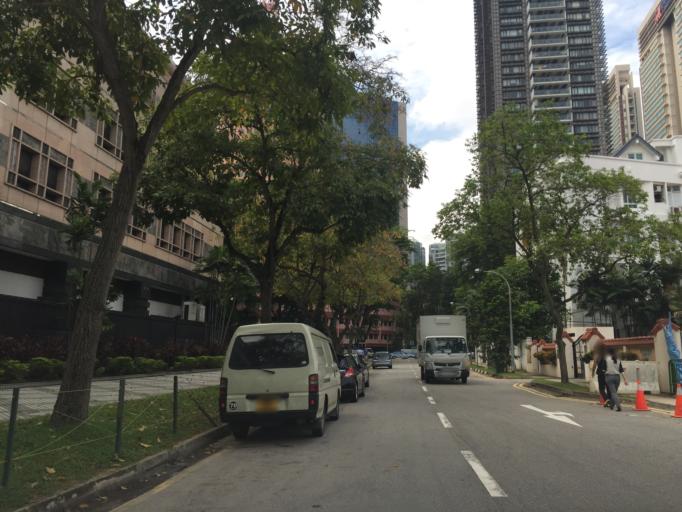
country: SG
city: Singapore
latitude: 1.3192
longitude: 103.8416
